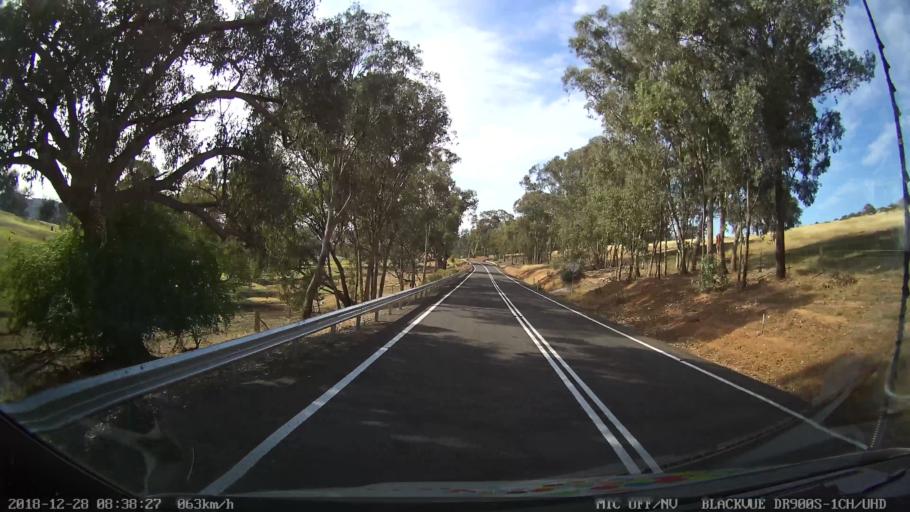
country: AU
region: New South Wales
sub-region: Blayney
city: Blayney
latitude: -34.0037
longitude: 149.3152
